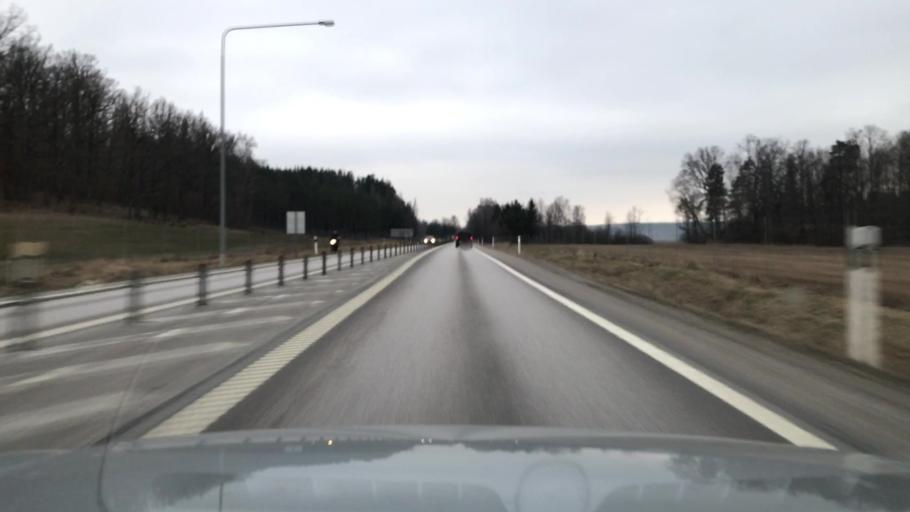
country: SE
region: OEstergoetland
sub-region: Valdemarsviks Kommun
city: Gusum
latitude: 58.3190
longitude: 16.4787
